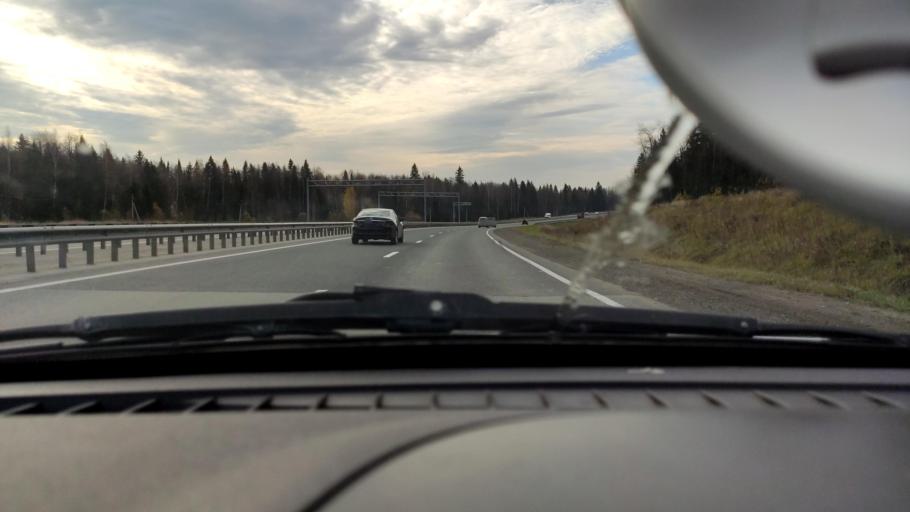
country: RU
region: Perm
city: Novyye Lyady
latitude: 58.0336
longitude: 56.4333
